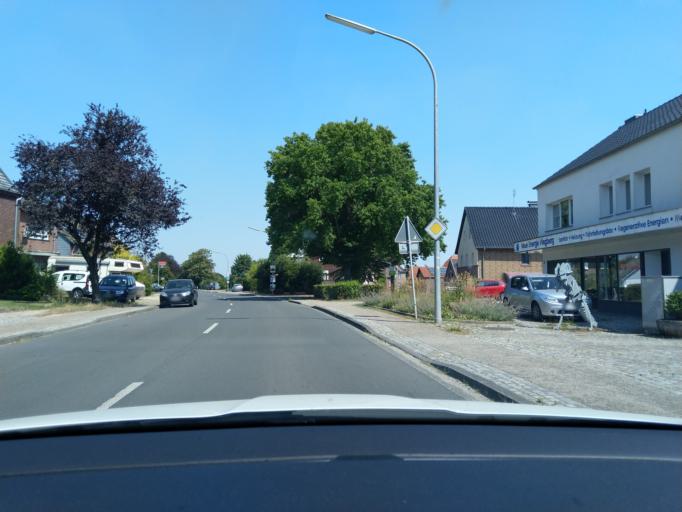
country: DE
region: North Rhine-Westphalia
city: Wegberg
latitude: 51.1371
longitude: 6.2602
